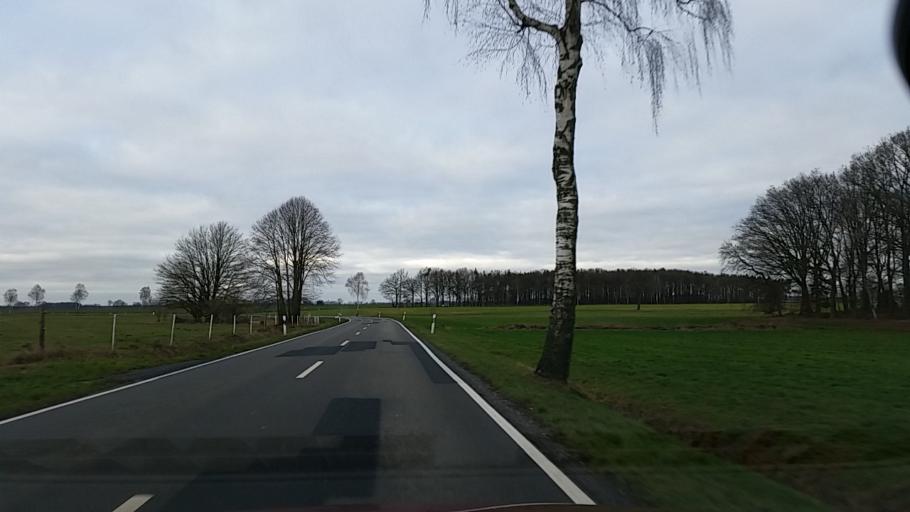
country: DE
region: Lower Saxony
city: Wittingen
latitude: 52.6930
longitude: 10.7487
